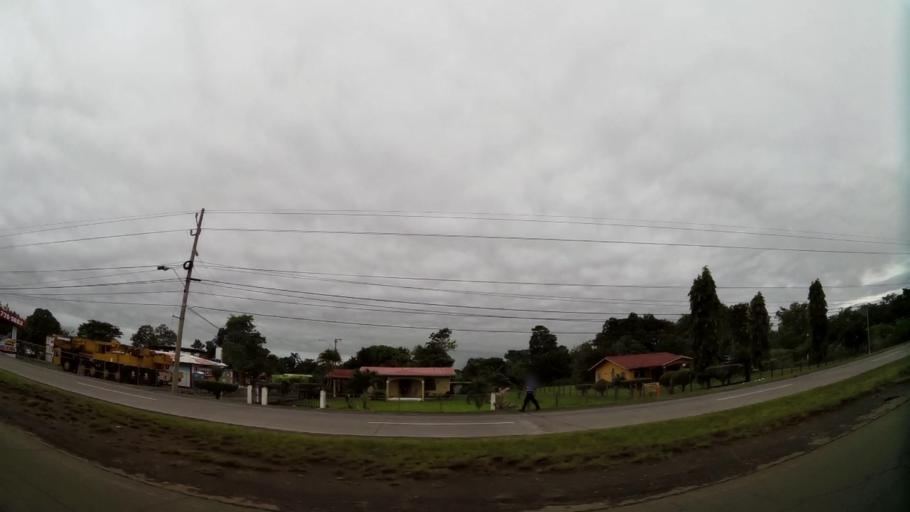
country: PA
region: Chiriqui
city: Boqueron
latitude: 8.4899
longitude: -82.5758
